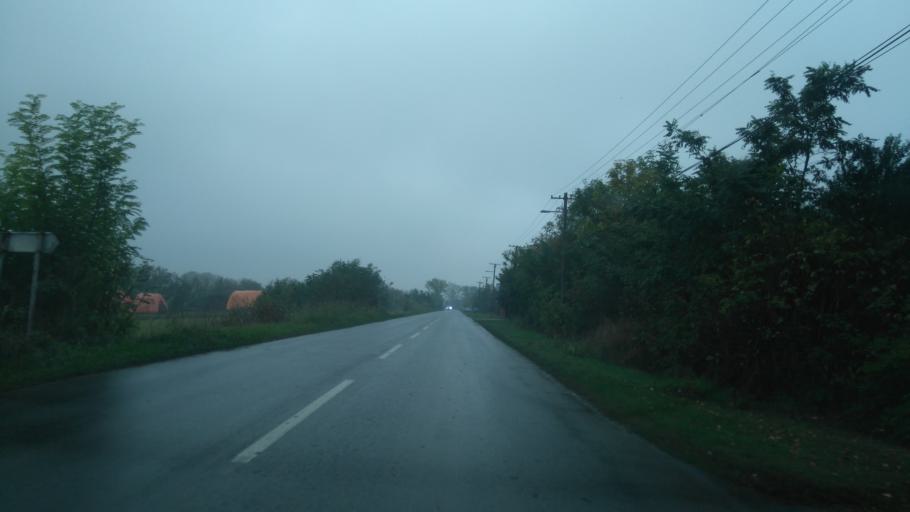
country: RS
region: Autonomna Pokrajina Vojvodina
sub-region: Juznobacki Okrug
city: Becej
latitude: 45.6482
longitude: 20.0340
